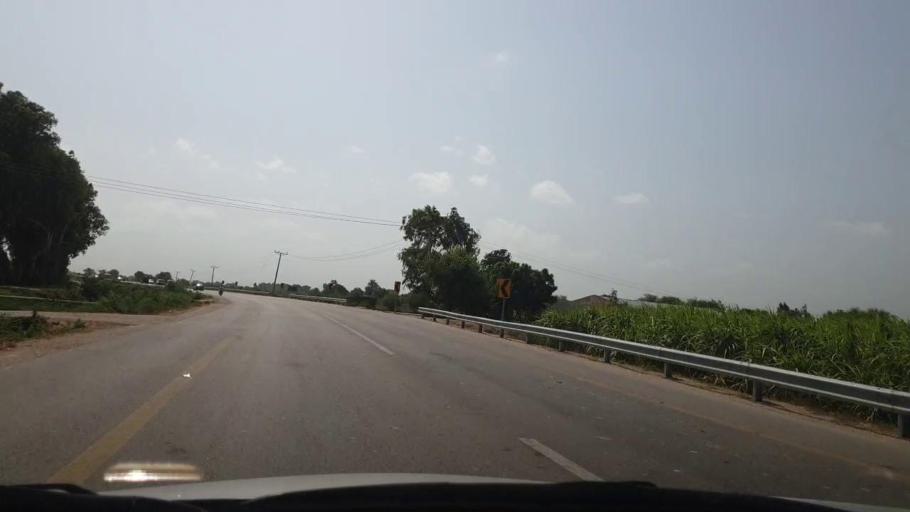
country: PK
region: Sindh
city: Matli
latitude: 24.9860
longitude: 68.6608
